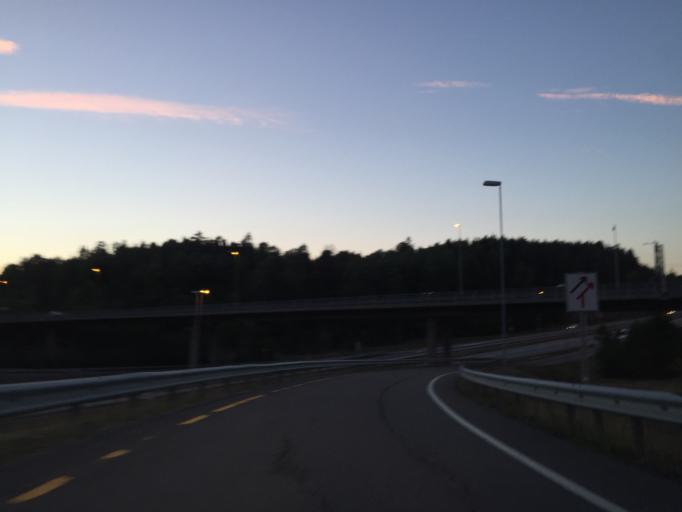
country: NO
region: Akershus
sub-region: Vestby
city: Vestby
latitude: 59.5158
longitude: 10.7256
